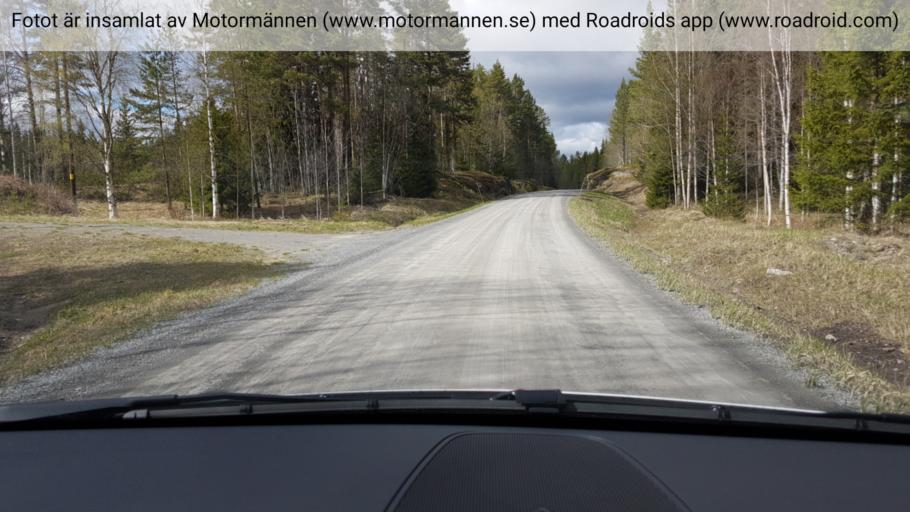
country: SE
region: Jaemtland
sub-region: OEstersunds Kommun
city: Brunflo
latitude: 63.1078
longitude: 15.0930
